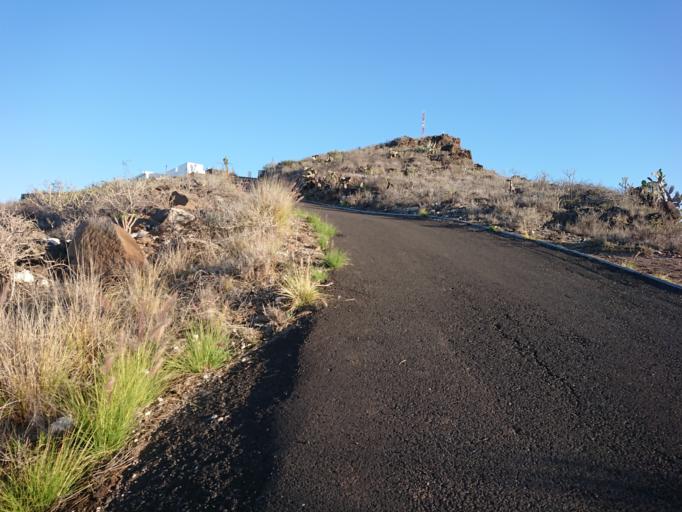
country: ES
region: Canary Islands
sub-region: Provincia de Santa Cruz de Tenerife
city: Tazacorte
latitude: 28.6597
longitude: -17.9436
